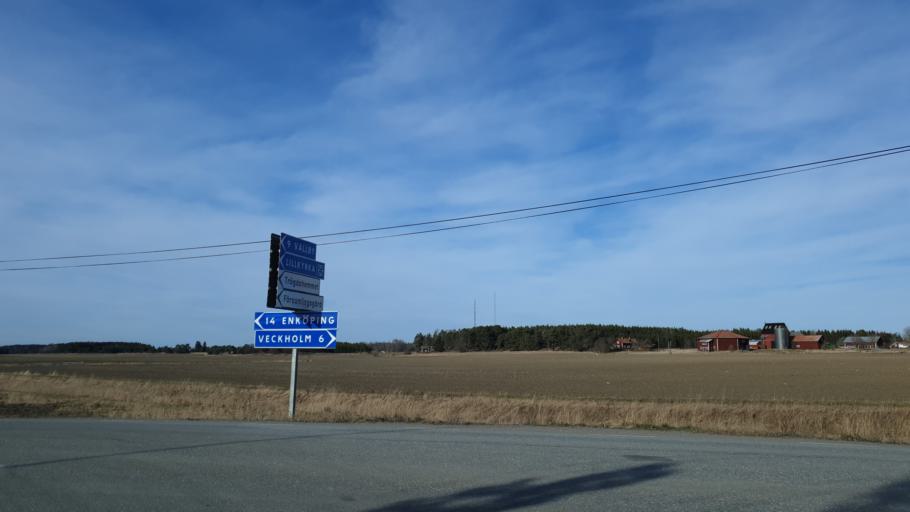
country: SE
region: Uppsala
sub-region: Enkopings Kommun
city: Grillby
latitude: 59.5611
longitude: 17.2470
